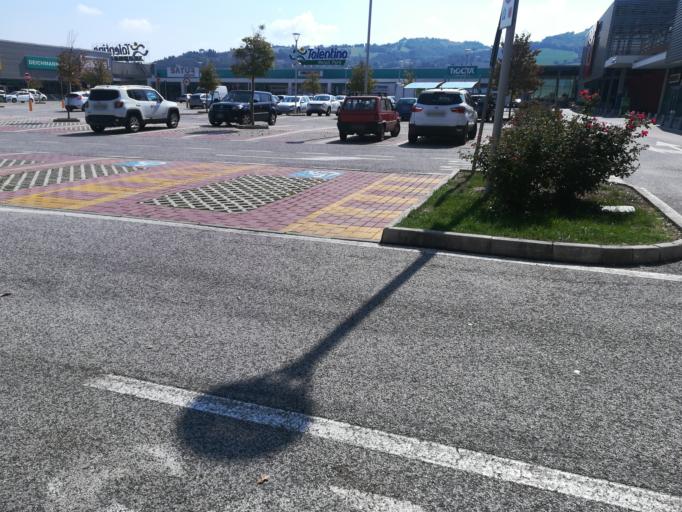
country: IT
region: The Marches
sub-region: Provincia di Macerata
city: Tolentino
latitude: 43.2176
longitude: 13.3084
